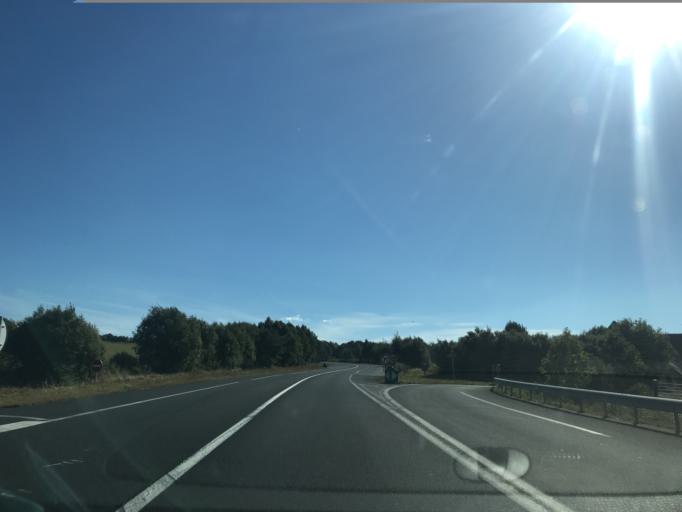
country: FR
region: Auvergne
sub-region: Departement du Puy-de-Dome
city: La Bourboule
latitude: 45.6663
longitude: 2.7278
